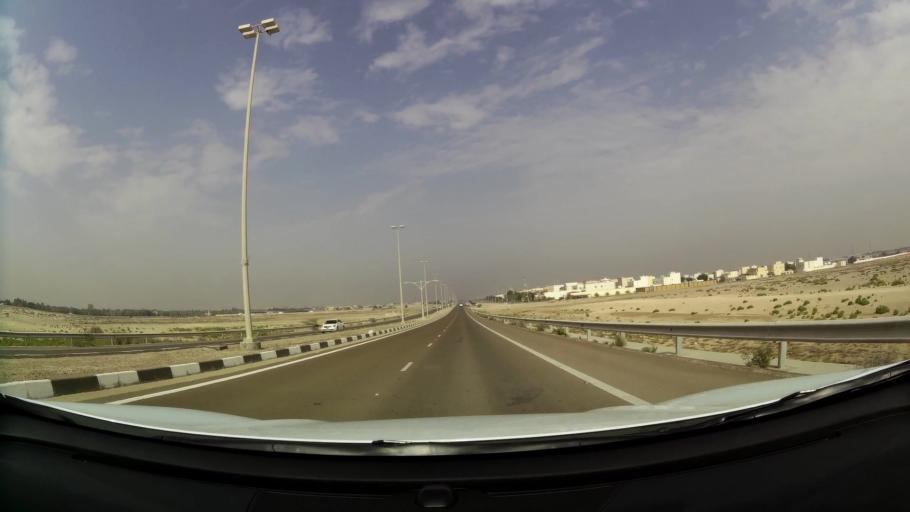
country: AE
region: Abu Dhabi
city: Abu Dhabi
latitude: 24.2787
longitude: 54.6636
